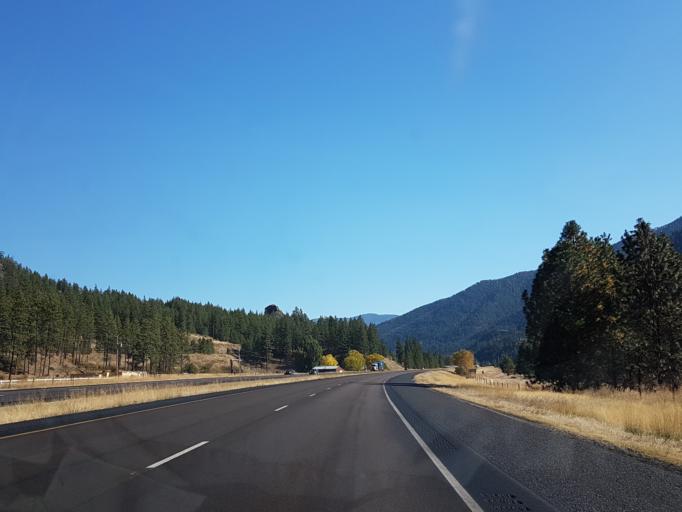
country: US
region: Montana
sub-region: Missoula County
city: Frenchtown
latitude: 47.0153
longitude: -114.5060
